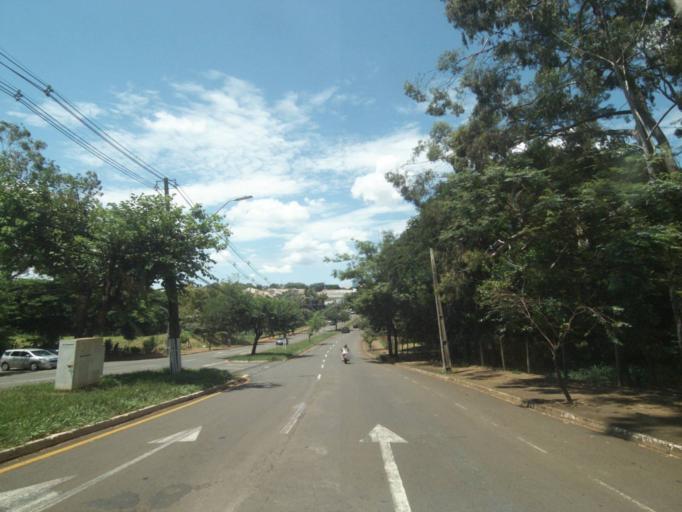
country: BR
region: Parana
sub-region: Londrina
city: Londrina
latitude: -23.3129
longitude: -51.2067
